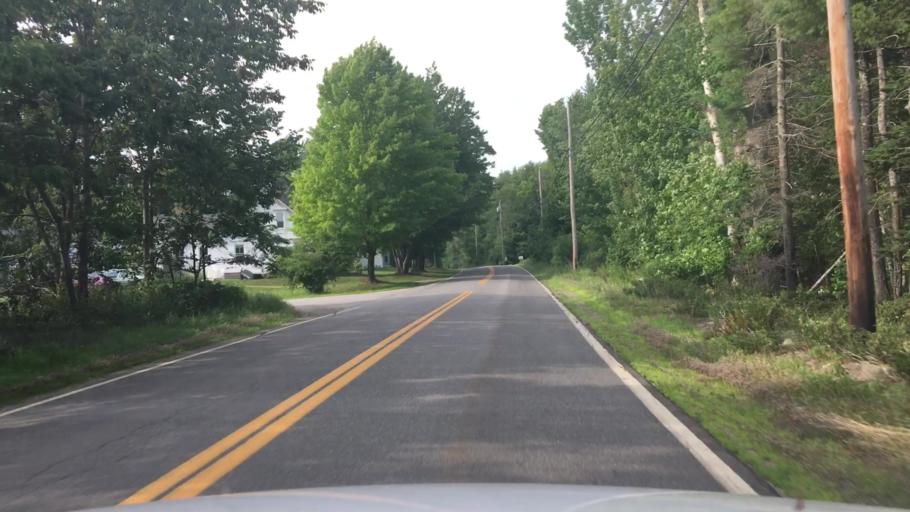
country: US
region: Maine
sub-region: Lincoln County
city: Waldoboro
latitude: 44.1472
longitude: -69.3742
